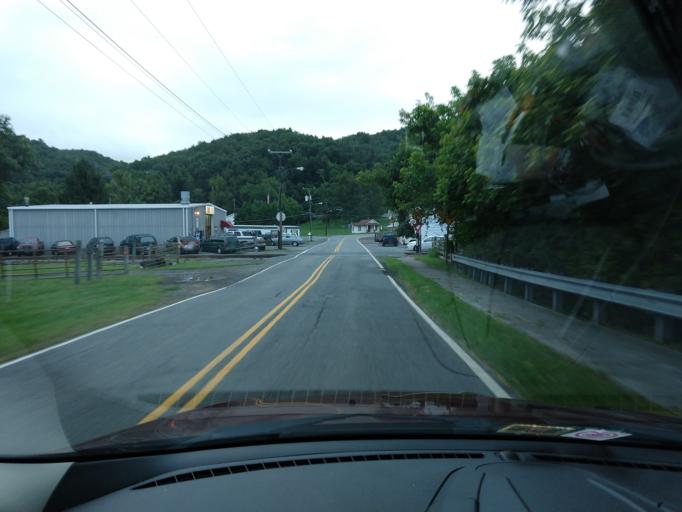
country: US
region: Virginia
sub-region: City of Covington
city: Fairlawn
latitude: 37.7625
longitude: -80.0008
